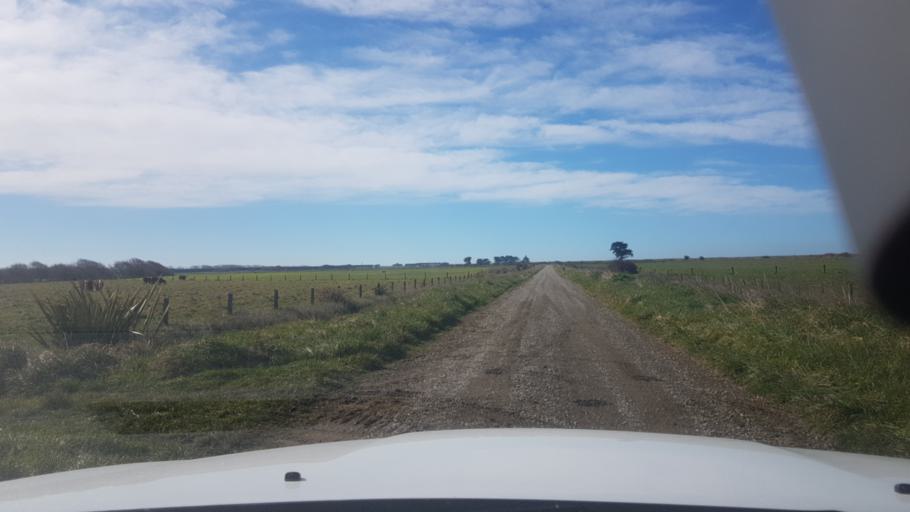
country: NZ
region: Canterbury
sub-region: Timaru District
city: Timaru
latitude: -44.2637
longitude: 171.3669
